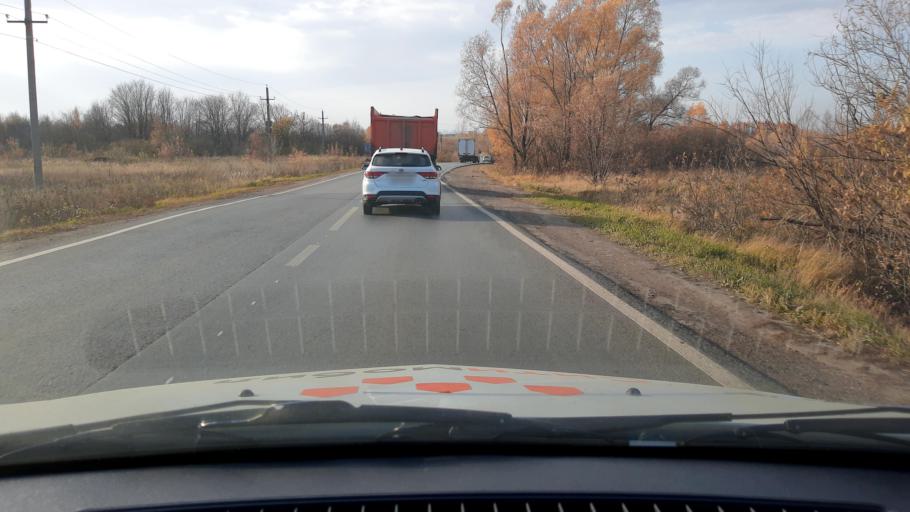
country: RU
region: Bashkortostan
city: Iglino
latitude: 54.7398
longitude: 56.2453
